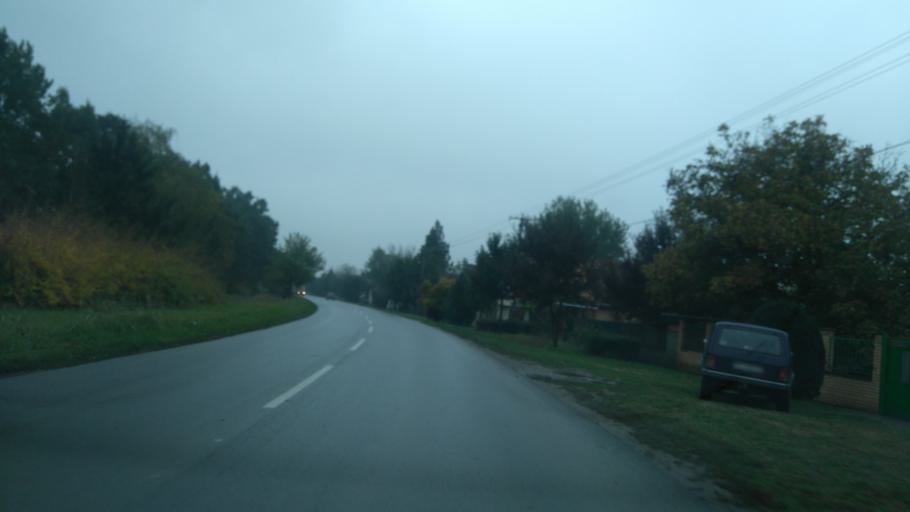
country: RS
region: Autonomna Pokrajina Vojvodina
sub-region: Juznobacki Okrug
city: Becej
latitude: 45.6409
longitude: 20.0279
